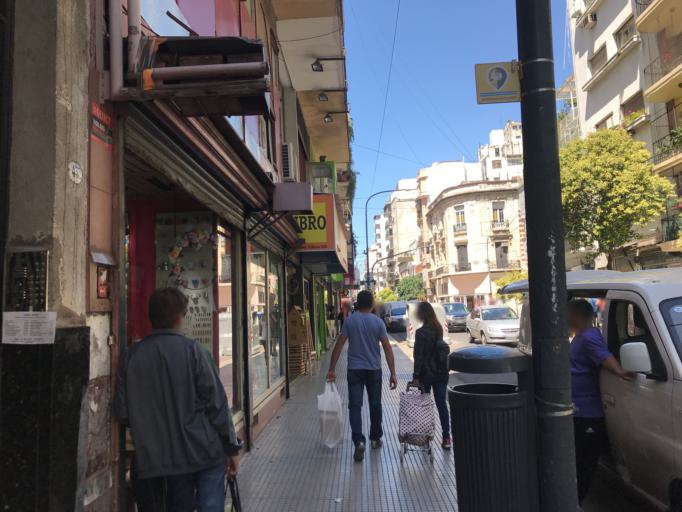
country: AR
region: Buenos Aires F.D.
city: Buenos Aires
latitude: -34.6040
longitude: -58.3984
